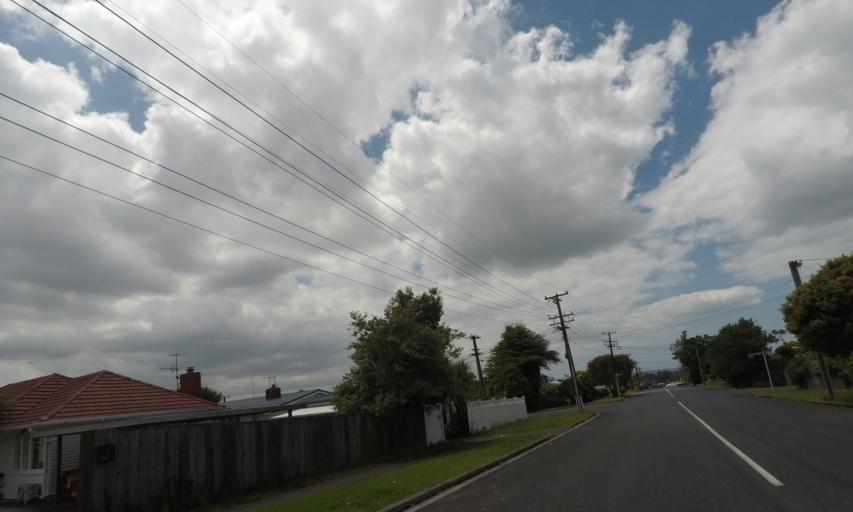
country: NZ
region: Auckland
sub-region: Auckland
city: Waitakere
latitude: -36.9054
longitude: 174.6691
